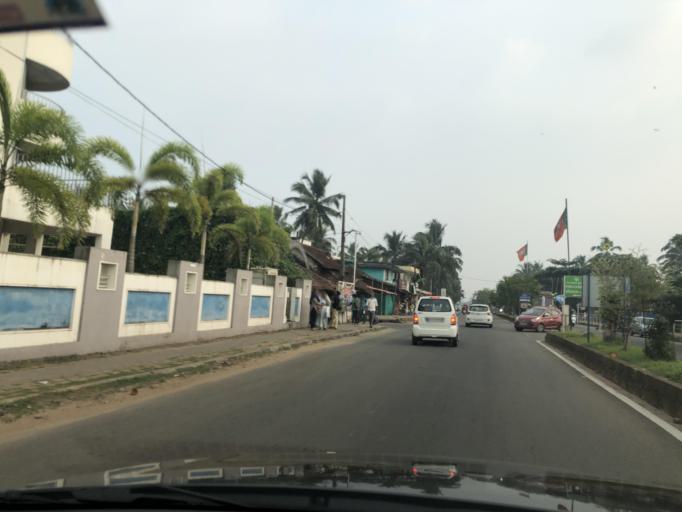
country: IN
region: Kerala
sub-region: Kozhikode
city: Kozhikode
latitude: 11.2749
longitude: 75.7643
